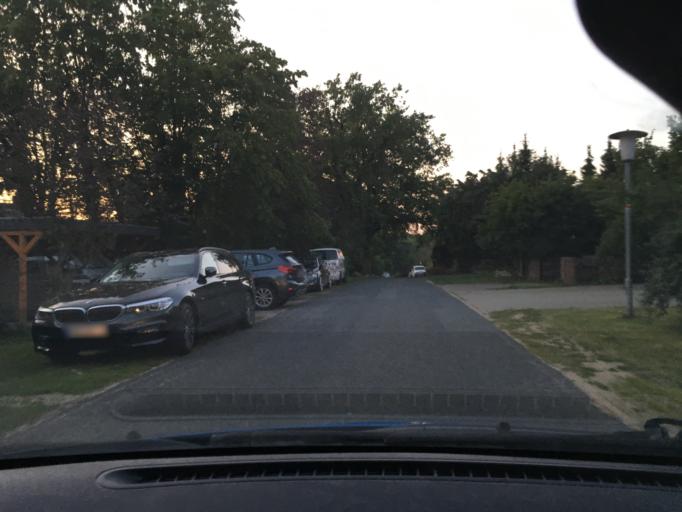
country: DE
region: Lower Saxony
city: Amelinghausen
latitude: 53.1262
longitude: 10.1905
